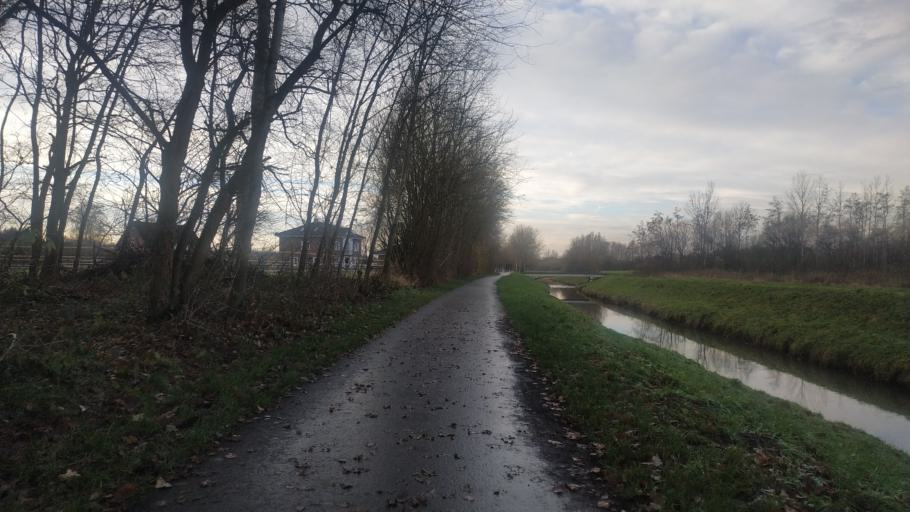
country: DE
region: North Rhine-Westphalia
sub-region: Regierungsbezirk Munster
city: Horstel
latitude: 52.2919
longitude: 7.6212
